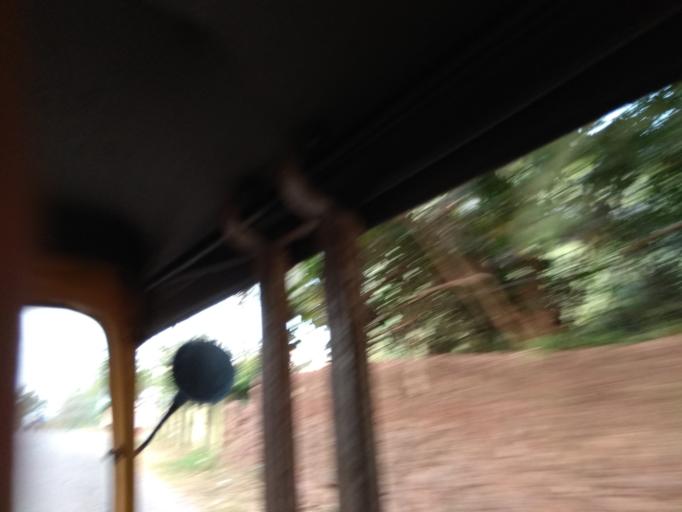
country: IN
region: Karnataka
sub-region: Dakshina Kannada
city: Mangalore
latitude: 12.9267
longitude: 74.8675
